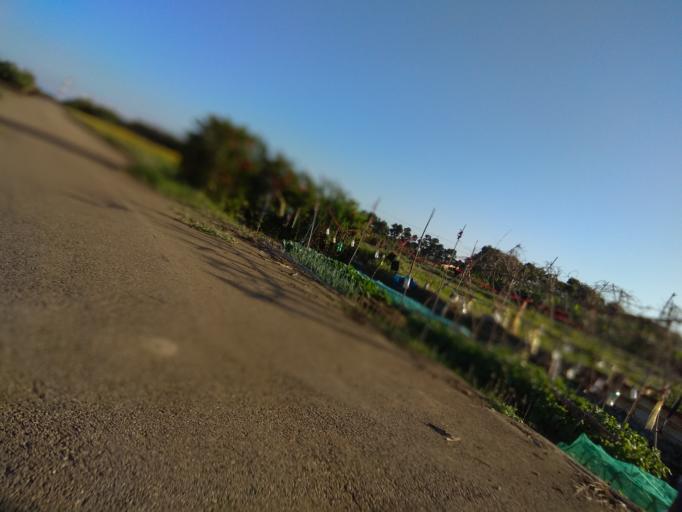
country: TW
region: Taiwan
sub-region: Hsinchu
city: Zhubei
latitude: 24.9947
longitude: 121.0531
